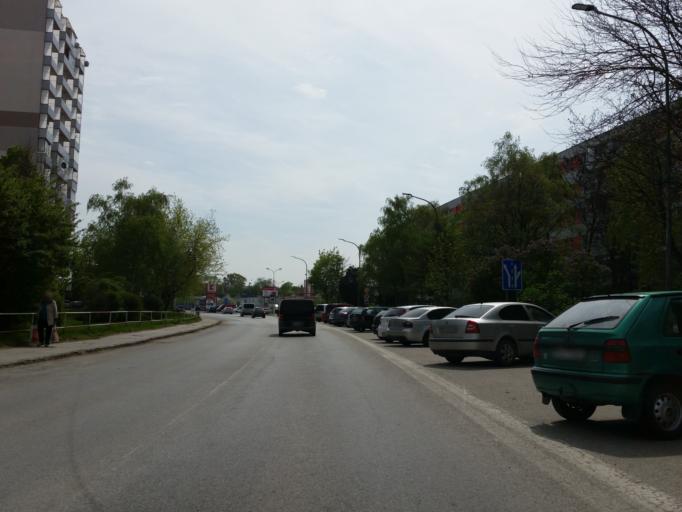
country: SK
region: Trnavsky
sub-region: Okres Galanta
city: Galanta
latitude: 48.2832
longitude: 17.7345
